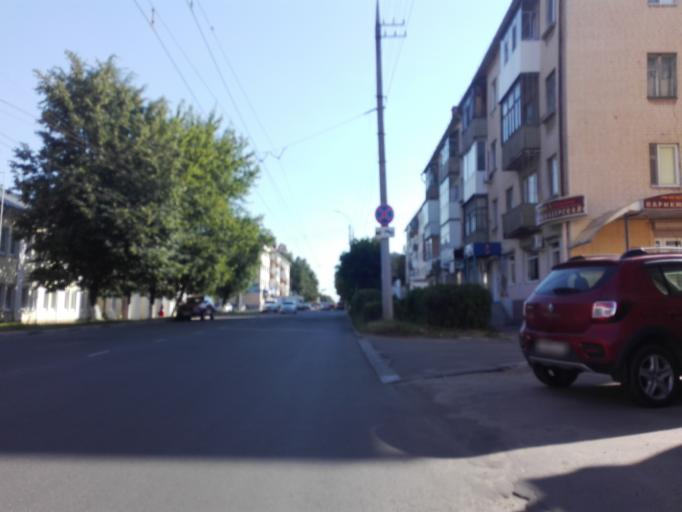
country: RU
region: Orjol
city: Orel
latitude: 52.9774
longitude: 36.0656
